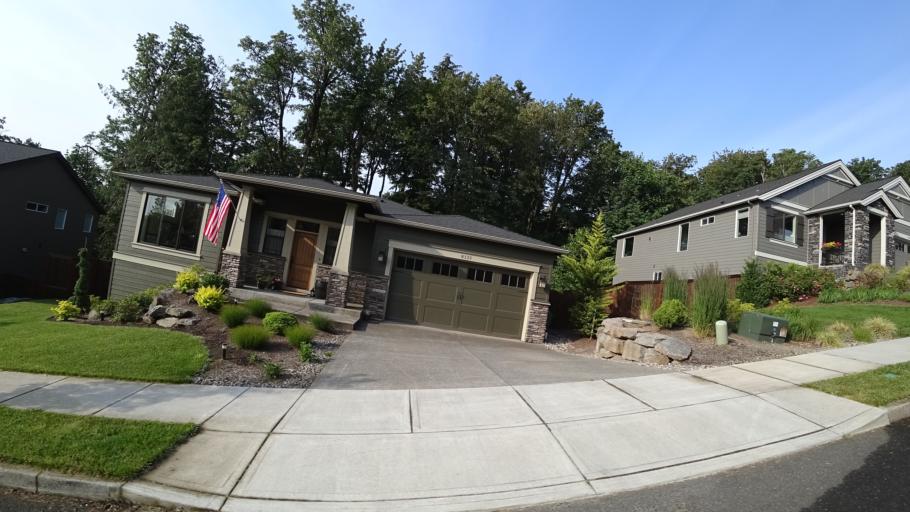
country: US
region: Oregon
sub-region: Clackamas County
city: Happy Valley
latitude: 45.4642
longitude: -122.5131
